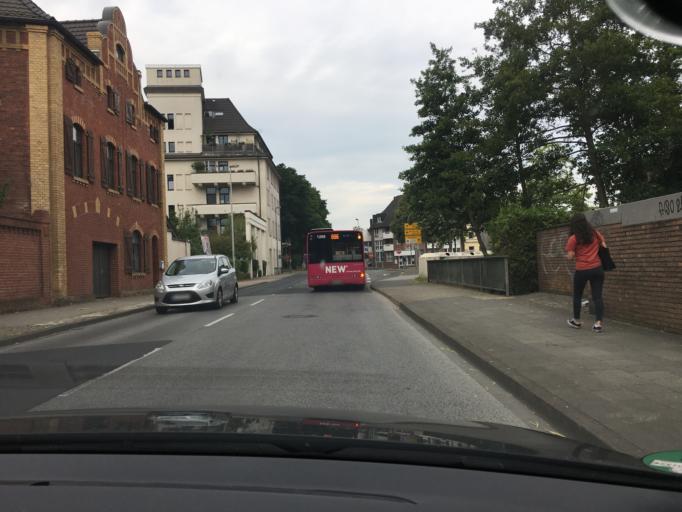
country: DE
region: North Rhine-Westphalia
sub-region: Regierungsbezirk Dusseldorf
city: Monchengladbach
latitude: 51.1271
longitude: 6.4129
